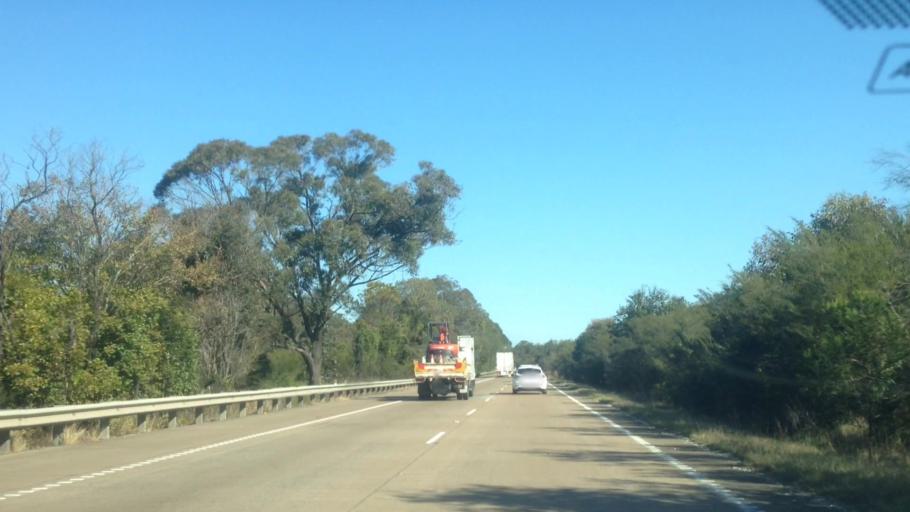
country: AU
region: New South Wales
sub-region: Wyong Shire
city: Charmhaven
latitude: -33.1663
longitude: 151.4683
